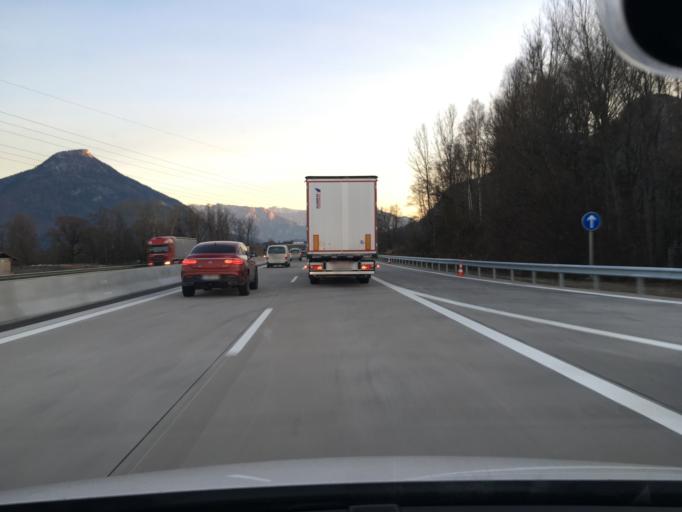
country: DE
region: Bavaria
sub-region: Upper Bavaria
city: Flintsbach
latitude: 47.7322
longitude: 12.1323
